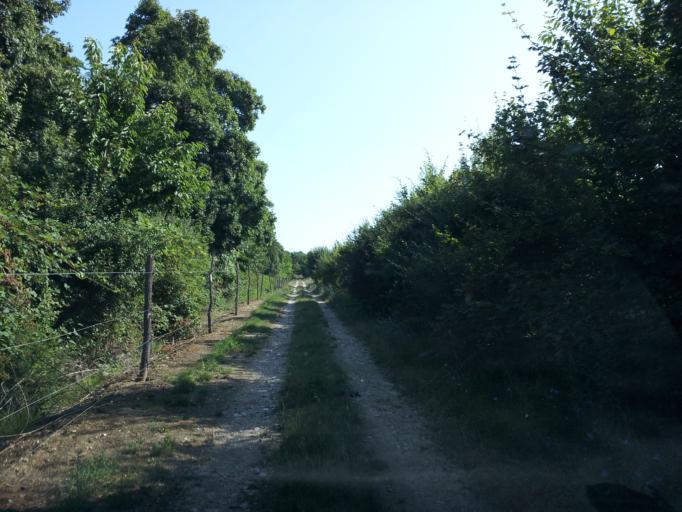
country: HU
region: Zala
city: Cserszegtomaj
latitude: 46.8551
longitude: 17.2222
